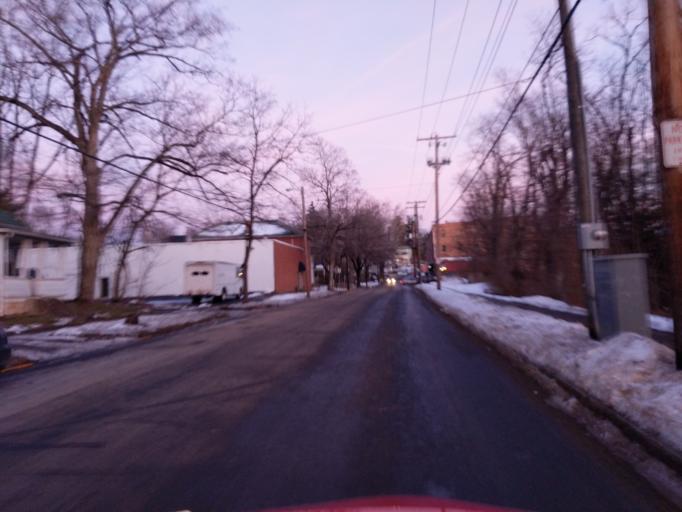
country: US
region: Ohio
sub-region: Athens County
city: Athens
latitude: 39.3335
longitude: -82.1126
